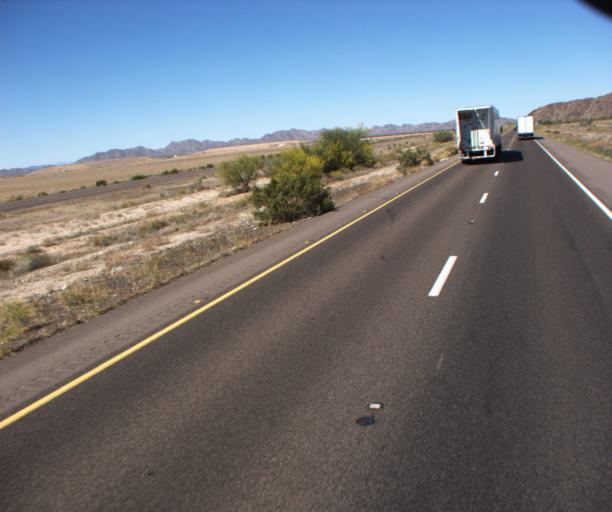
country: US
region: Arizona
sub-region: Maricopa County
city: Gila Bend
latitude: 33.1536
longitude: -112.6499
